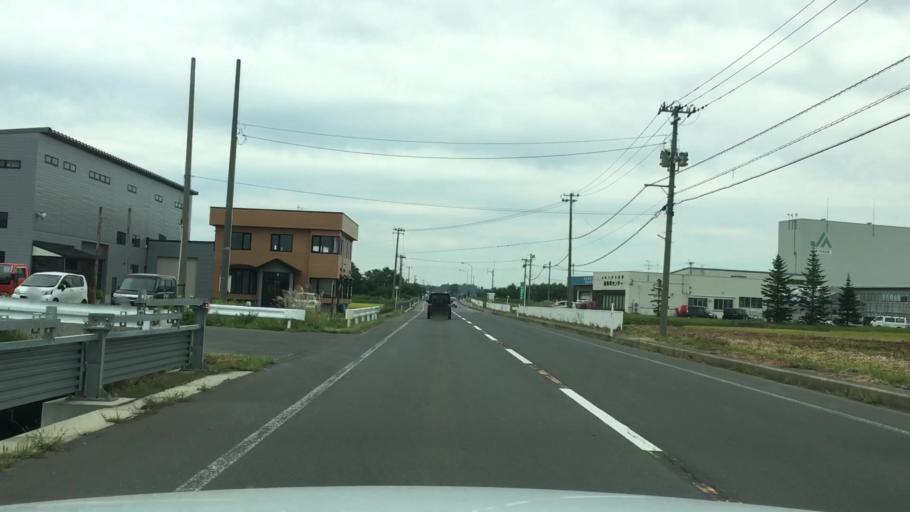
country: JP
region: Aomori
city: Hirosaki
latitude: 40.6351
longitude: 140.4495
